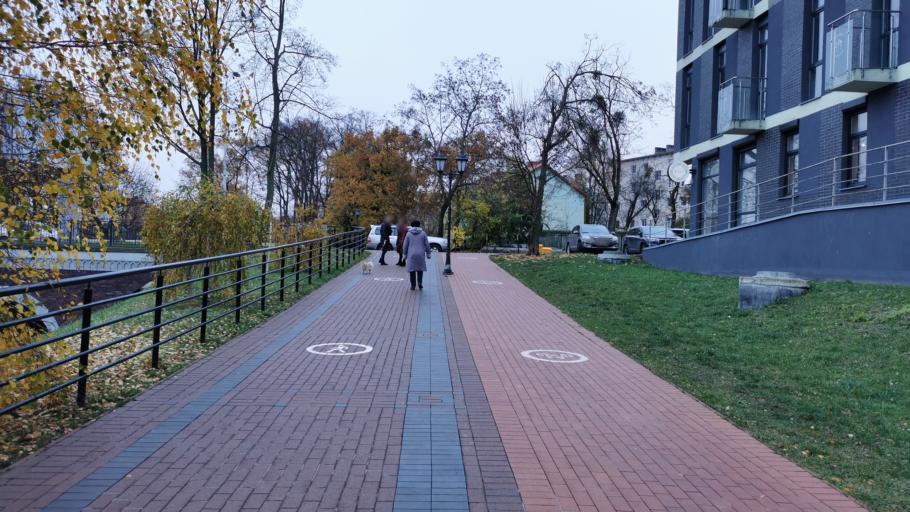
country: RU
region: Kaliningrad
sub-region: Gorod Kaliningrad
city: Kaliningrad
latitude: 54.7333
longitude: 20.5304
